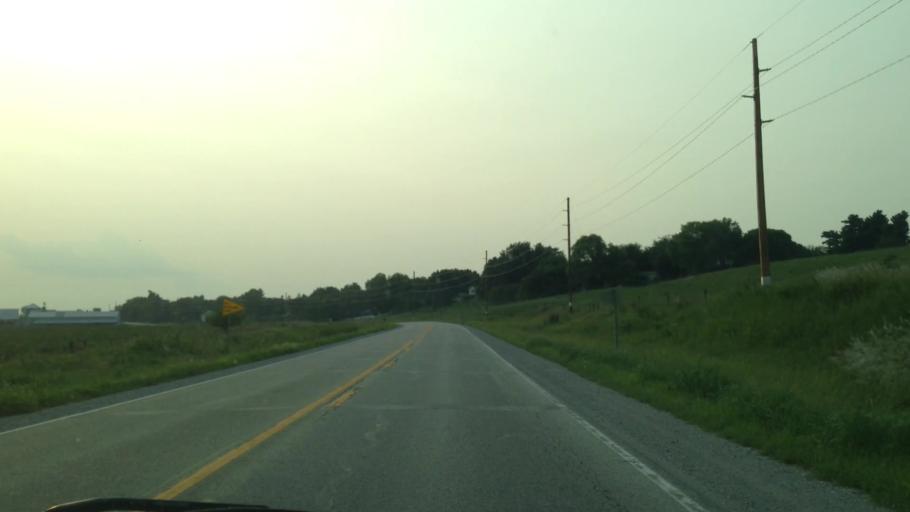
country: US
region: Iowa
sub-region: Benton County
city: Walford
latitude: 41.8001
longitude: -91.9326
